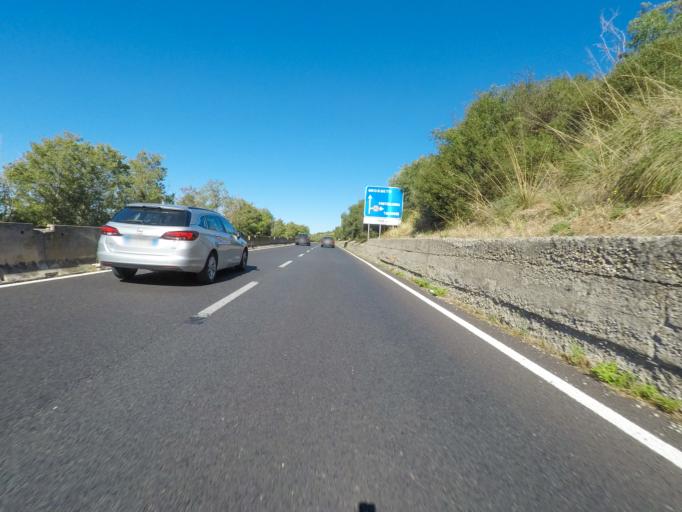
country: IT
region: Tuscany
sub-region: Provincia di Grosseto
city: Fonteblanda
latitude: 42.5597
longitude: 11.1721
